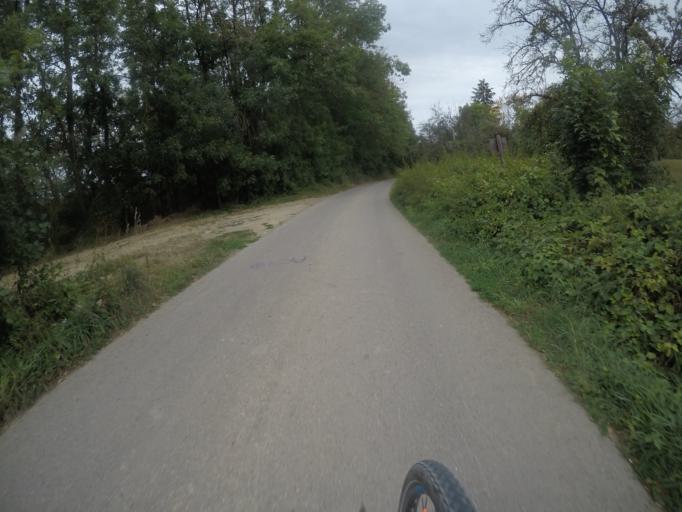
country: DE
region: Baden-Wuerttemberg
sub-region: Regierungsbezirk Stuttgart
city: Oberriexingen
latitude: 48.9241
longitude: 9.0317
